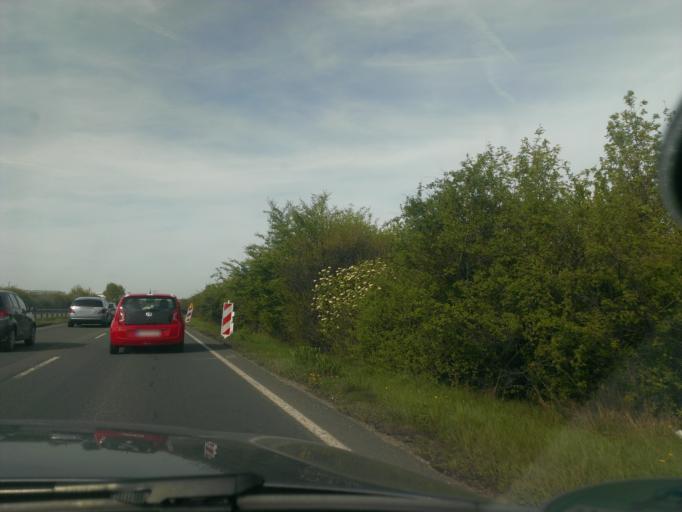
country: DE
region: Thuringia
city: Erfurt
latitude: 50.9642
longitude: 11.0894
